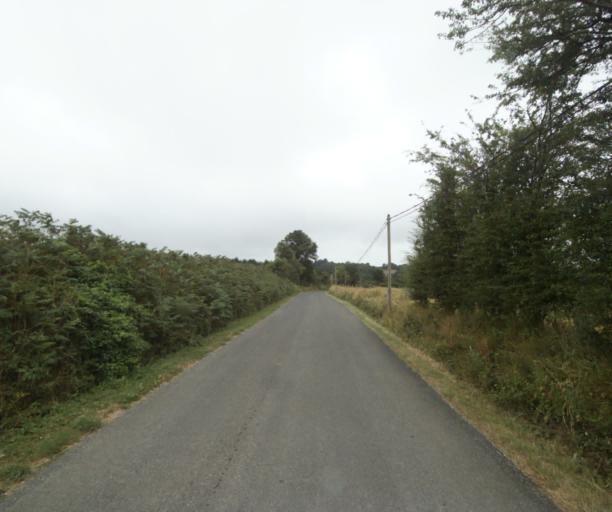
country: FR
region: Midi-Pyrenees
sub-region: Departement du Tarn
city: Soreze
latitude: 43.4063
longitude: 2.0580
